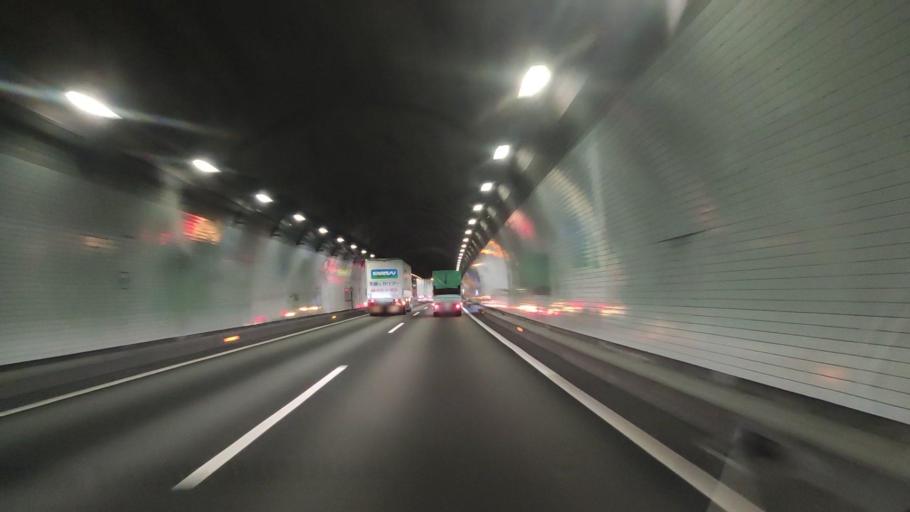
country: JP
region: Tokyo
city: Fussa
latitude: 35.7582
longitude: 139.2854
